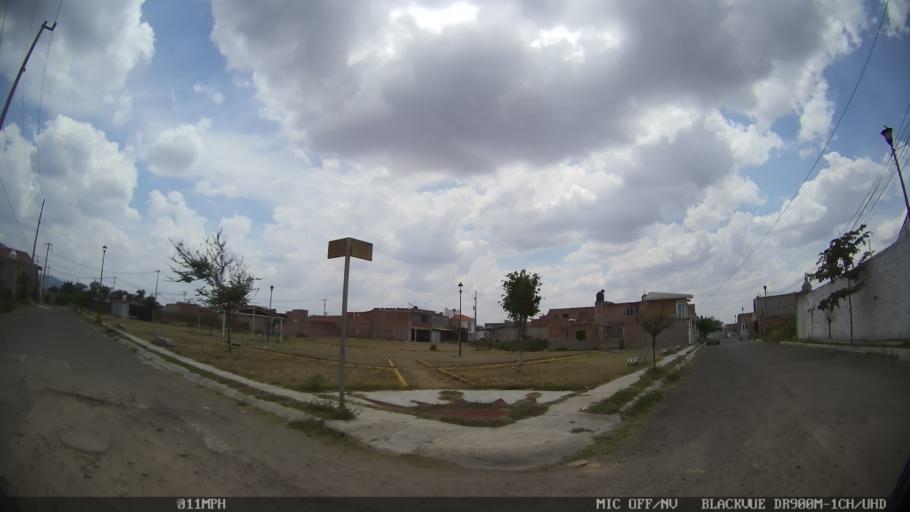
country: MX
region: Jalisco
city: Tonala
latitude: 20.6729
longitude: -103.2338
